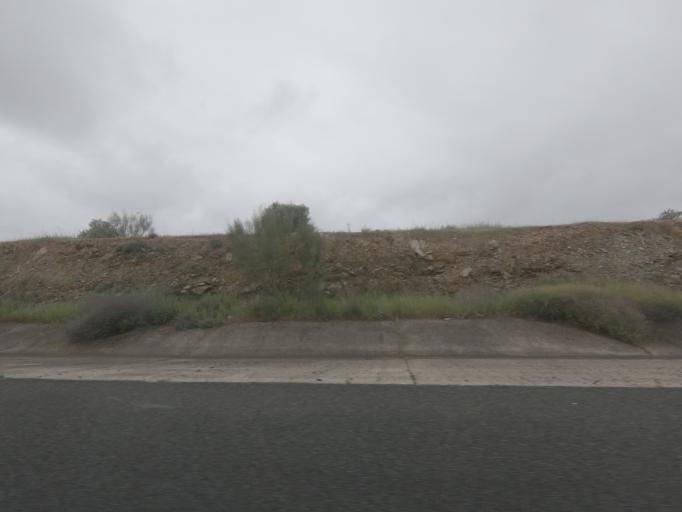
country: ES
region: Extremadura
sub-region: Provincia de Caceres
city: Hinojal
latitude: 39.6994
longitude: -6.4025
